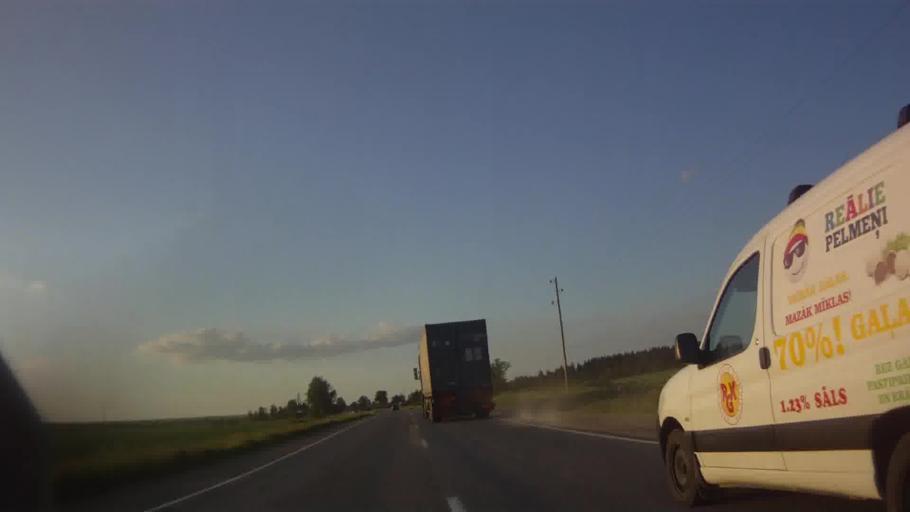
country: LV
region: Salas
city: Sala
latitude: 56.5731
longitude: 25.7766
